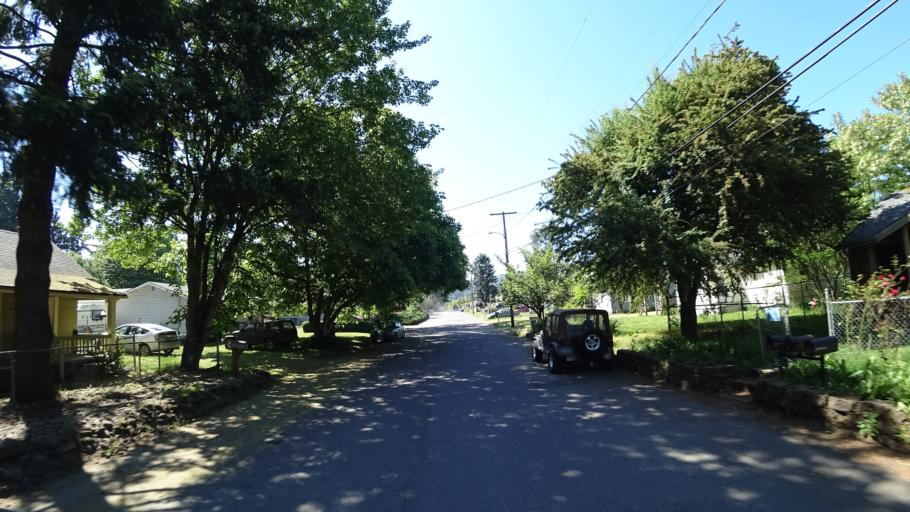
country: US
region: Oregon
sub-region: Multnomah County
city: Lents
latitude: 45.4820
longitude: -122.5450
